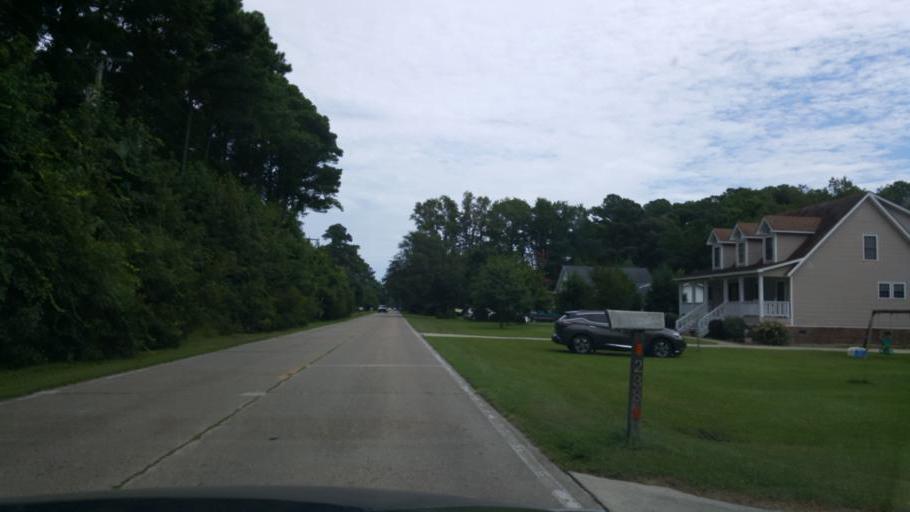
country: US
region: North Carolina
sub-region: Dare County
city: Manteo
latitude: 35.9259
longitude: -75.7008
